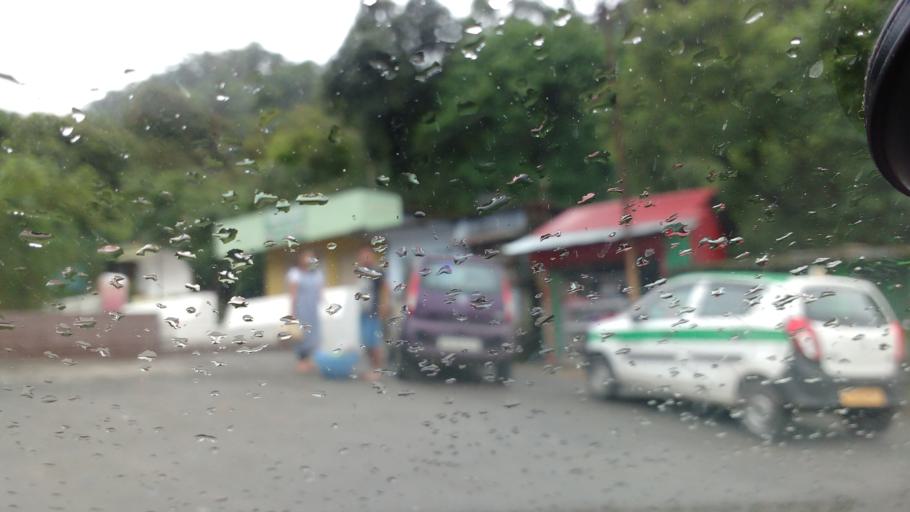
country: IN
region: Meghalaya
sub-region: East Khasi Hills
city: Cherrapunji
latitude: 25.2443
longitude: 91.7242
